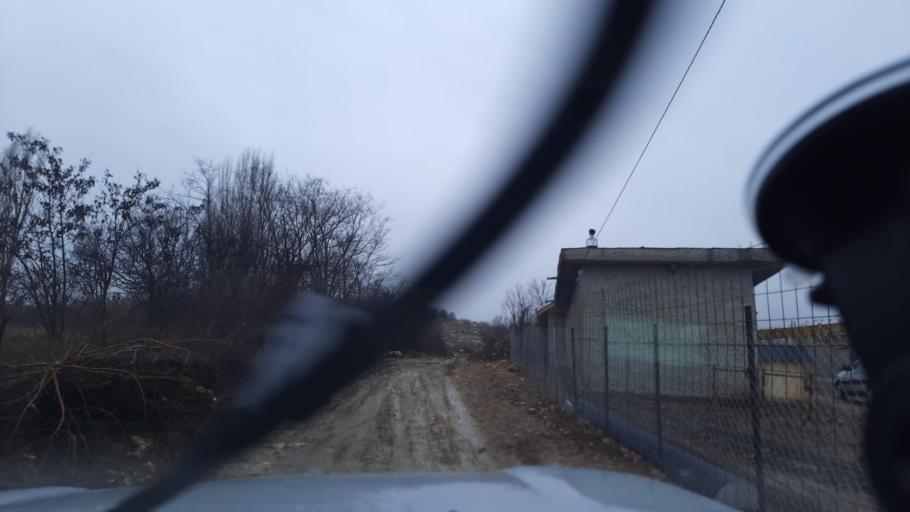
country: MK
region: Opstina Lipkovo
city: Matejche
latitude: 42.1250
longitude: 21.5868
